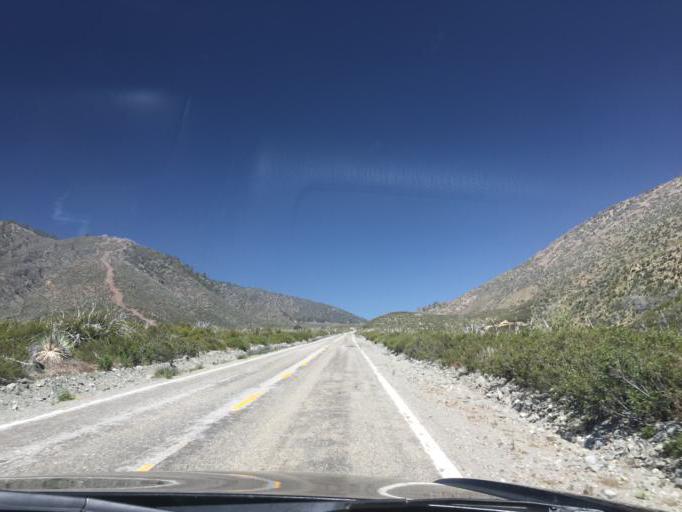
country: US
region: California
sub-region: San Bernardino County
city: Wrightwood
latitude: 34.3289
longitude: -117.5757
